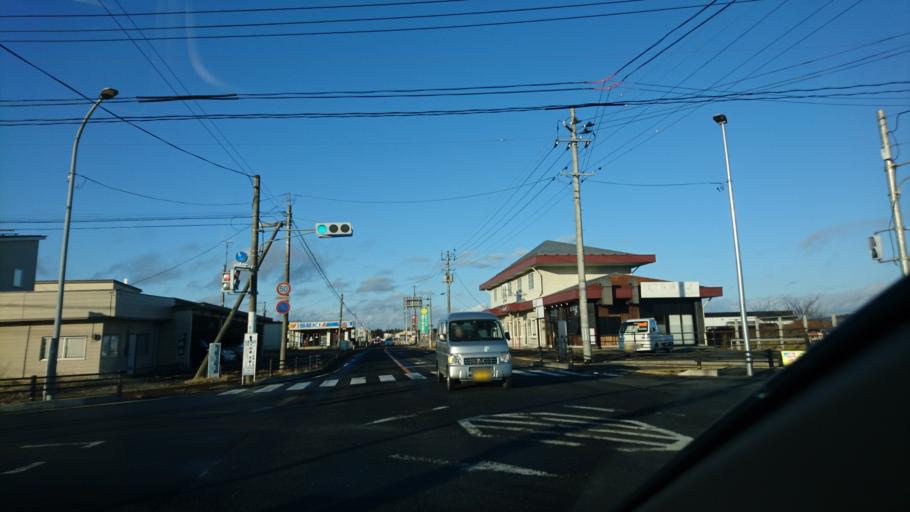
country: JP
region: Miyagi
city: Furukawa
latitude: 38.5767
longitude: 140.8601
